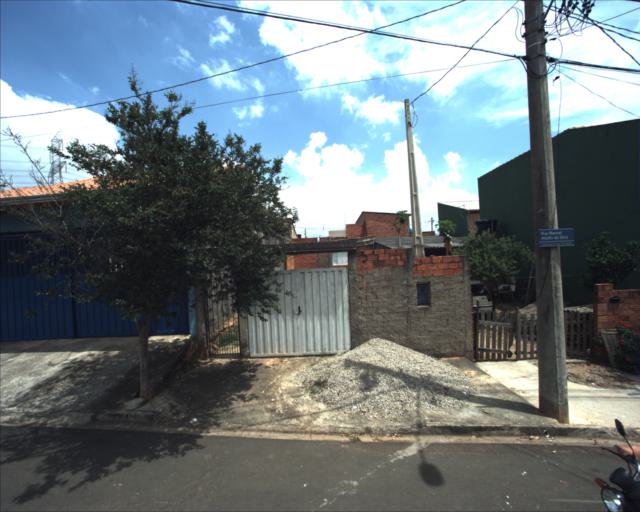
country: BR
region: Sao Paulo
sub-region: Sorocaba
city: Sorocaba
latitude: -23.4191
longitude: -47.4311
